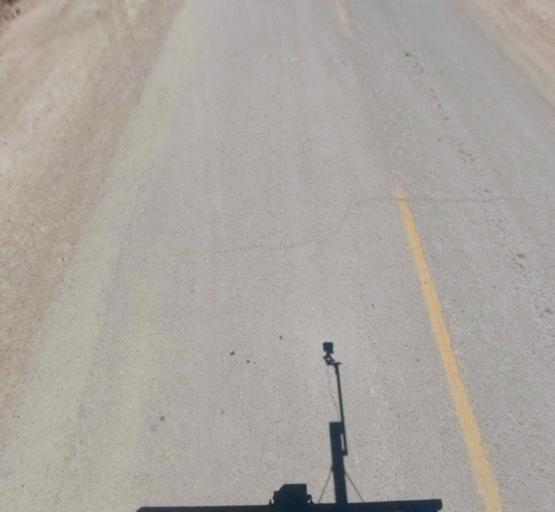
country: US
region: California
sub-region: Merced County
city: Dos Palos
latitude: 37.0546
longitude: -120.4548
